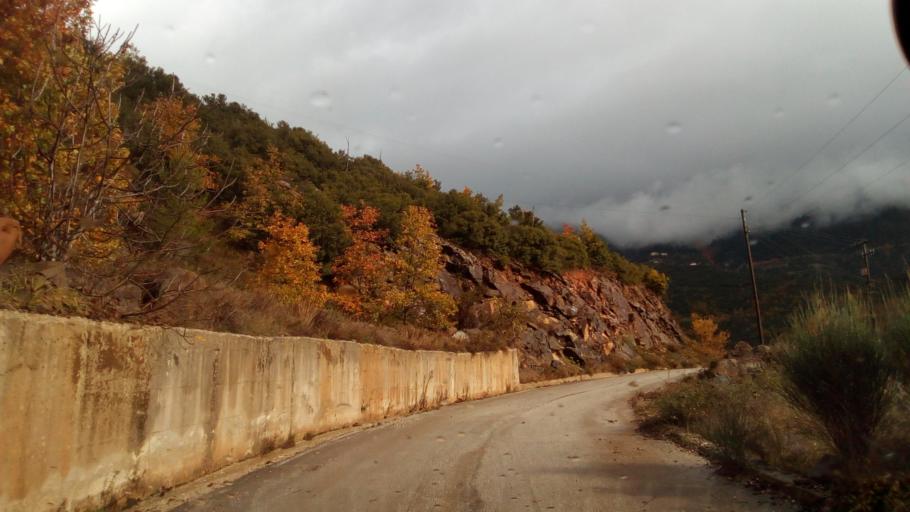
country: GR
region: West Greece
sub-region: Nomos Aitolias kai Akarnanias
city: Thermo
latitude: 38.6736
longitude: 21.8556
